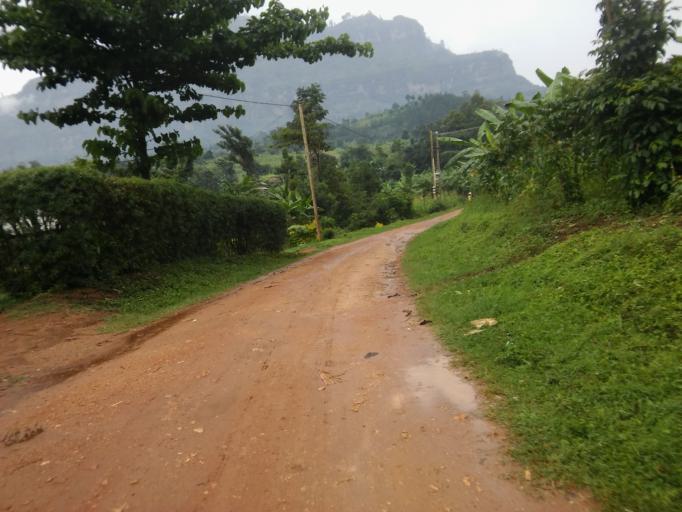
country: UG
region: Eastern Region
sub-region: Bududa District
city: Bududa
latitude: 0.9933
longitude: 34.2330
